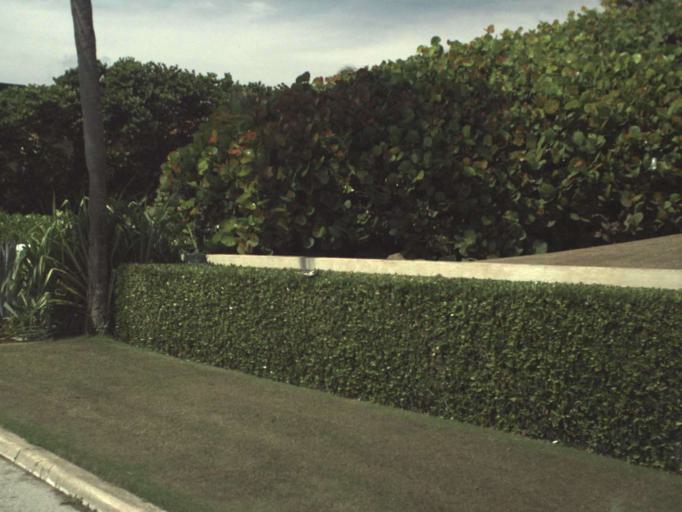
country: US
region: Florida
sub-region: Palm Beach County
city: Lake Clarke Shores
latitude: 26.6597
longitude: -80.0369
